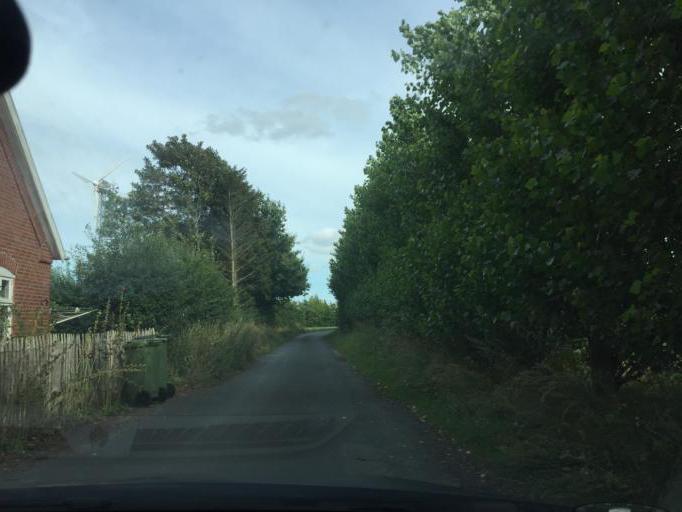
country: DK
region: South Denmark
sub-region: Kerteminde Kommune
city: Langeskov
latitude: 55.3462
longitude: 10.5201
